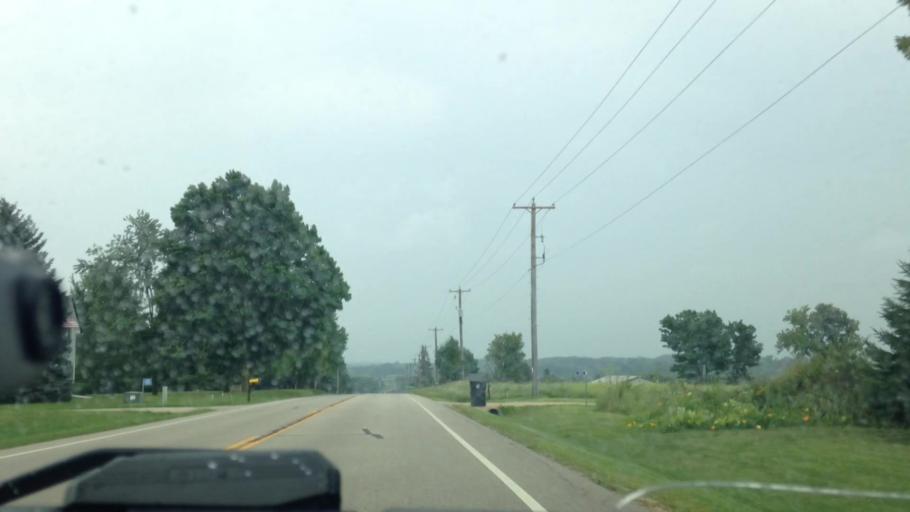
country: US
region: Wisconsin
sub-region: Washington County
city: Hartford
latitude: 43.4077
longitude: -88.3687
